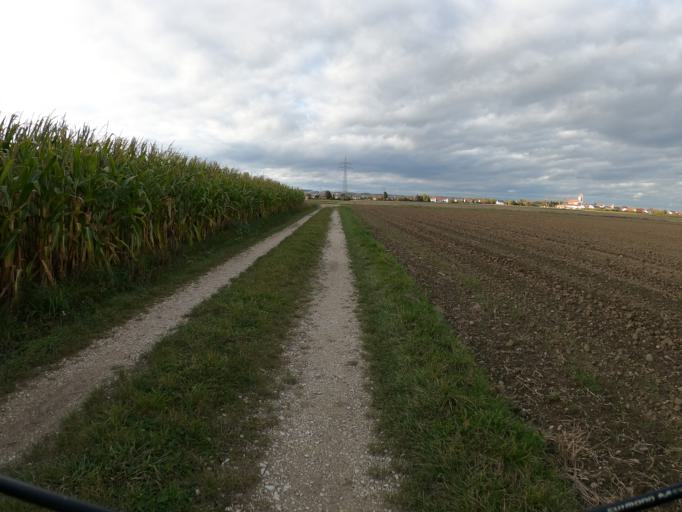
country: DE
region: Bavaria
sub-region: Swabia
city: Nersingen
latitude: 48.4177
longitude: 10.1255
